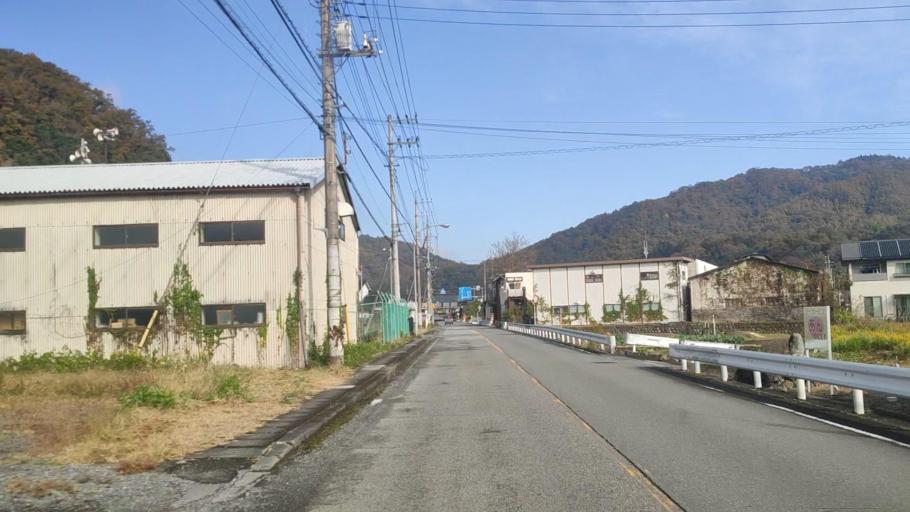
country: JP
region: Yamanashi
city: Ryuo
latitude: 35.4914
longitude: 138.4499
